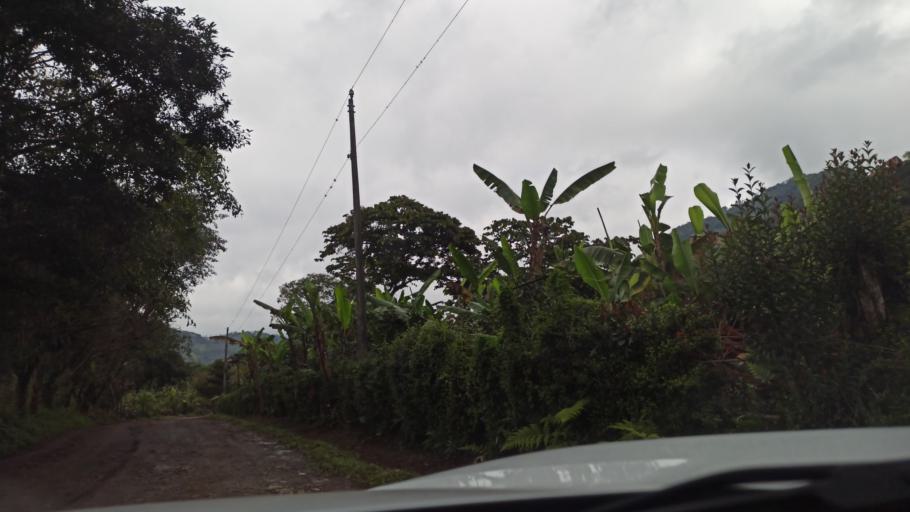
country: MX
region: Veracruz
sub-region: Fortin
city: Santa Lucia Potrerillo
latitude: 18.9702
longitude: -97.0269
